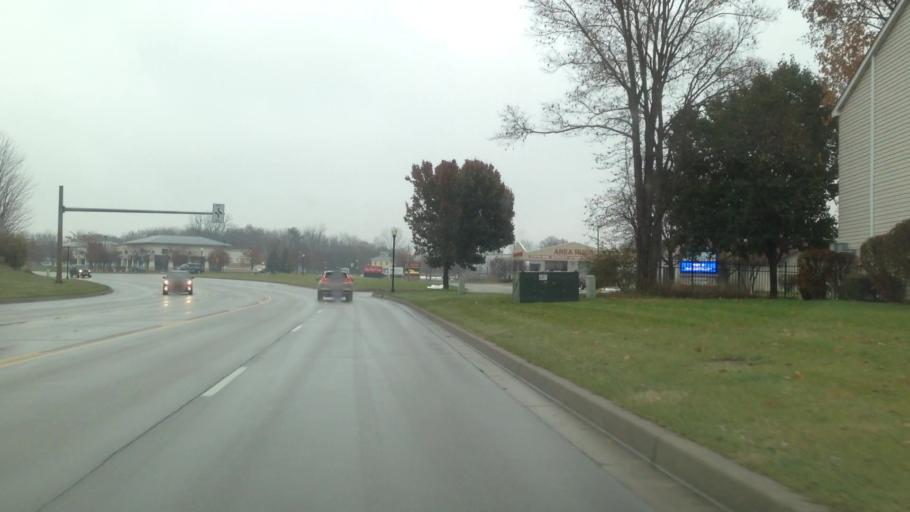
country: US
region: Indiana
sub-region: Saint Joseph County
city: Mishawaka
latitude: 41.7204
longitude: -86.1688
